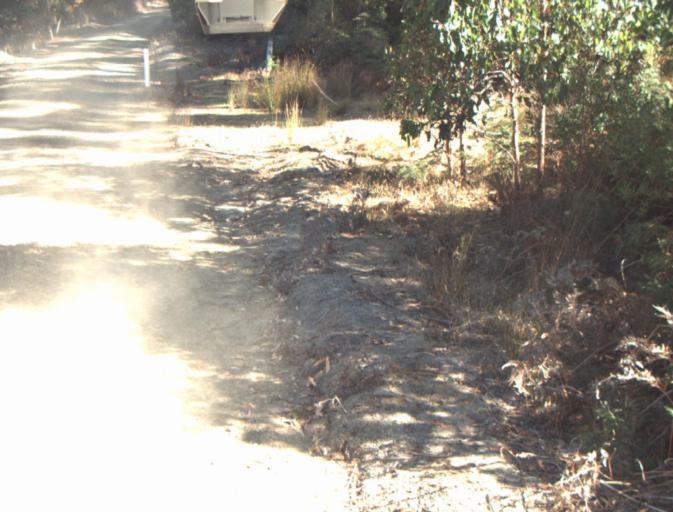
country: AU
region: Tasmania
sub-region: Dorset
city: Scottsdale
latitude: -41.3003
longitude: 147.3556
